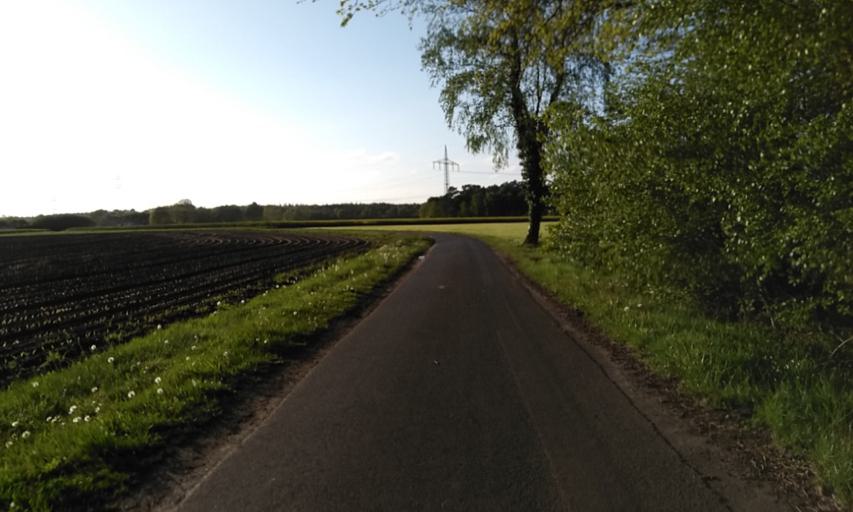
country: DE
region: Lower Saxony
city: Harsefeld
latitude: 53.4069
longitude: 9.5094
